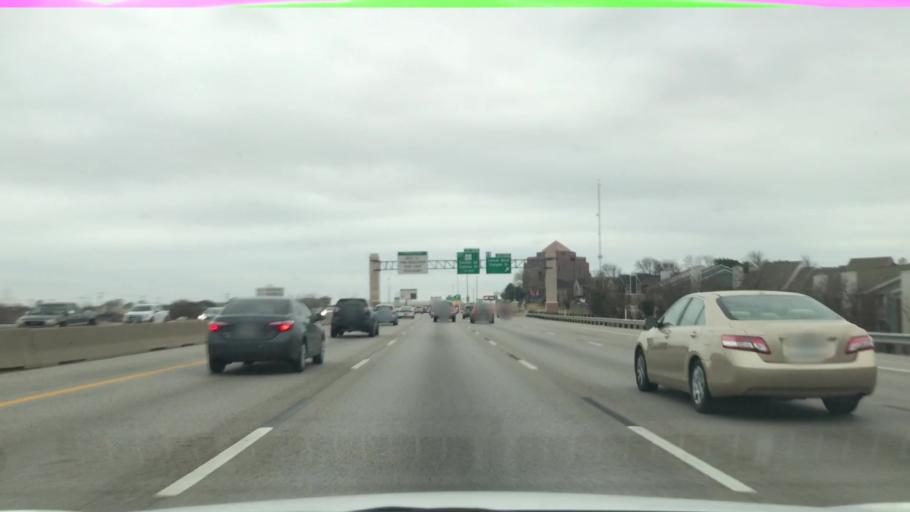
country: US
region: Texas
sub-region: Tarrant County
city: Arlington
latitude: 32.7595
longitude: -97.1211
